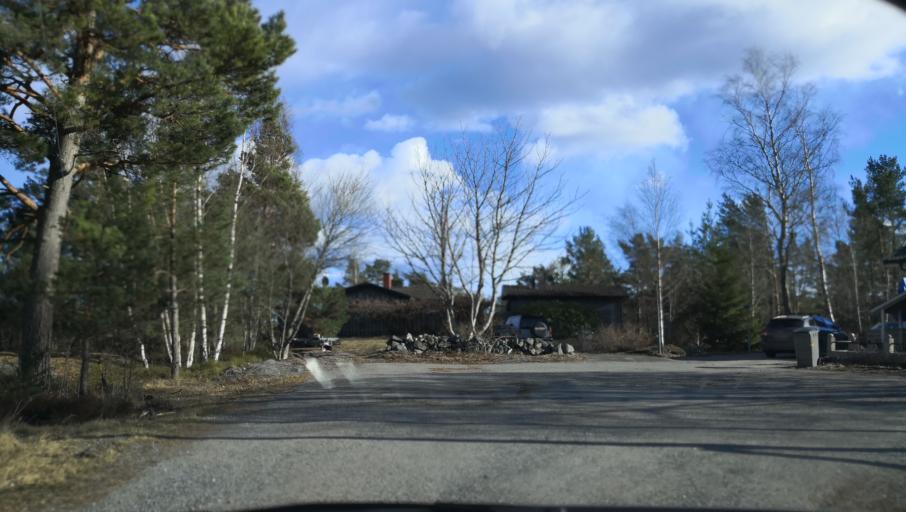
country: SE
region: Stockholm
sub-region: Varmdo Kommun
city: Hemmesta
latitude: 59.2446
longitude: 18.5187
